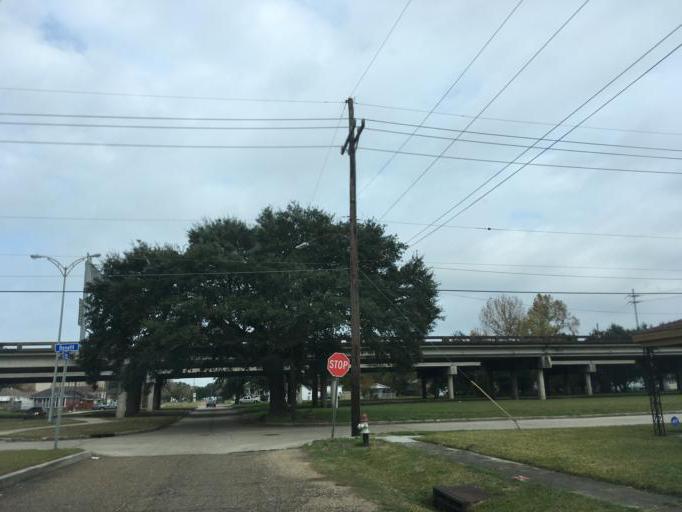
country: US
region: Louisiana
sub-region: Orleans Parish
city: New Orleans
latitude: 29.9903
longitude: -90.0632
